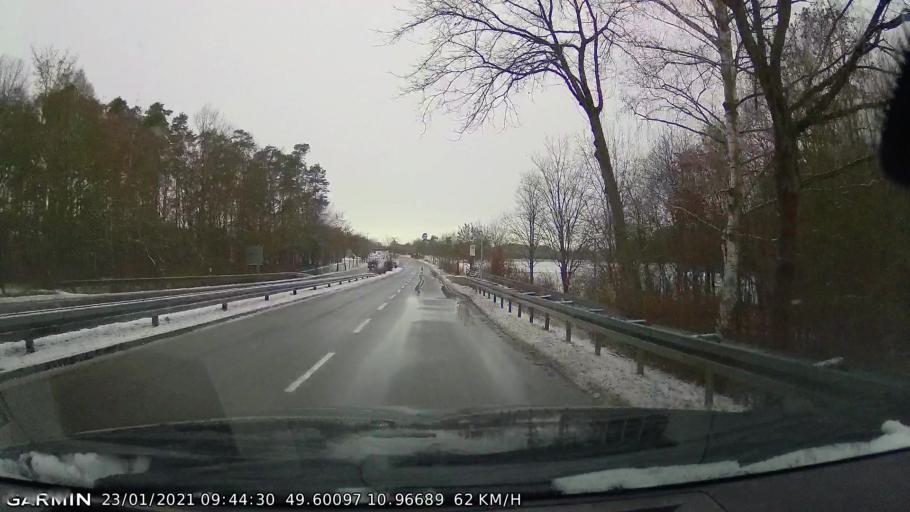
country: DE
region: Bavaria
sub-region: Regierungsbezirk Mittelfranken
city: Erlangen
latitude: 49.6010
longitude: 10.9669
